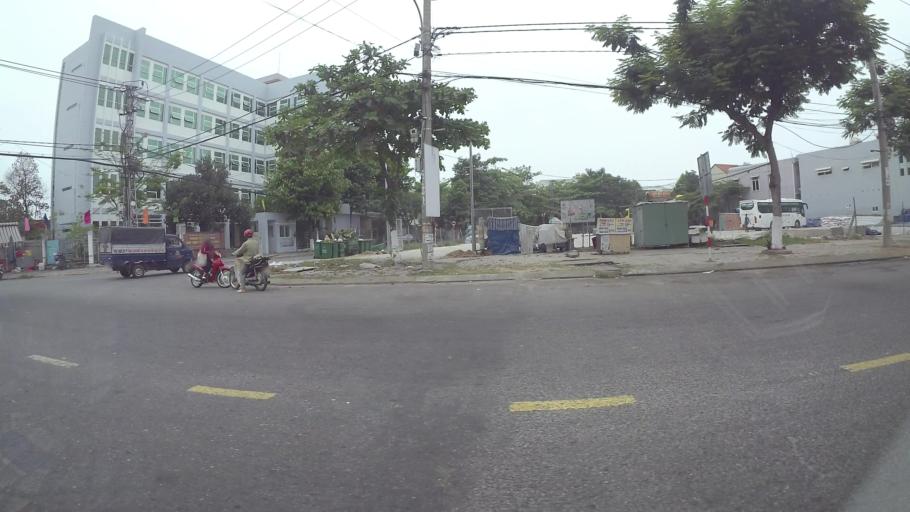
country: VN
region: Da Nang
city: Cam Le
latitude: 16.0249
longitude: 108.2101
